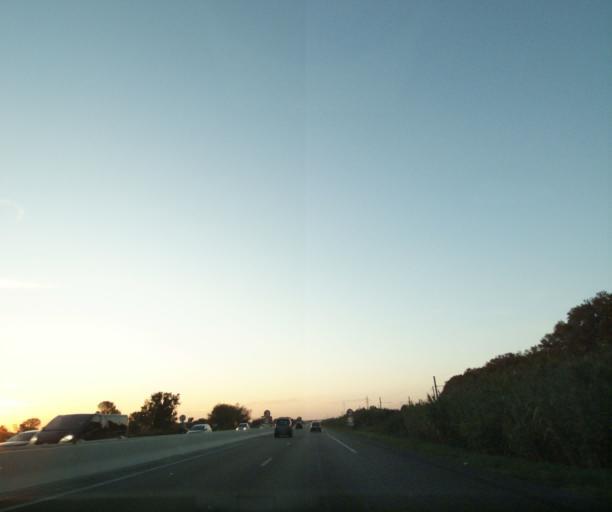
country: FR
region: Provence-Alpes-Cote d'Azur
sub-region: Departement des Bouches-du-Rhone
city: Arles
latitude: 43.6505
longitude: 4.6762
